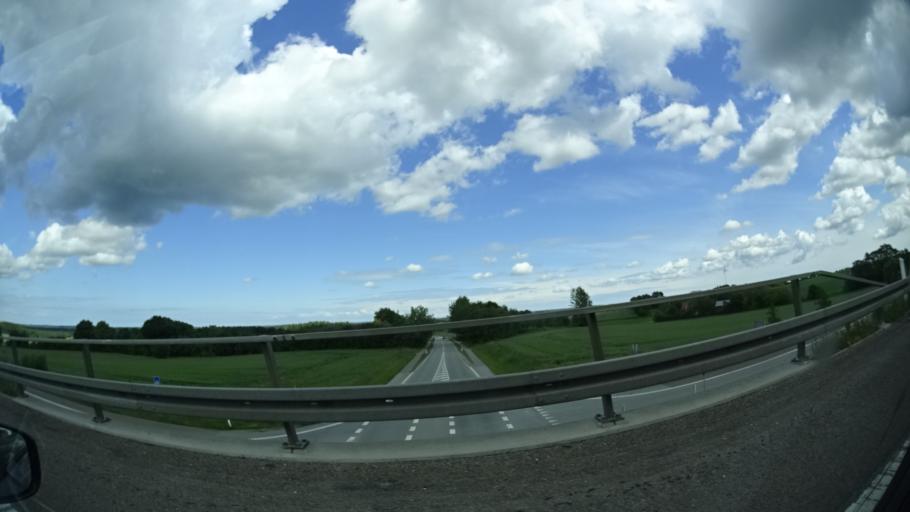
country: DK
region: Central Jutland
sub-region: Syddjurs Kommune
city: Ronde
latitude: 56.3033
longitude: 10.5067
